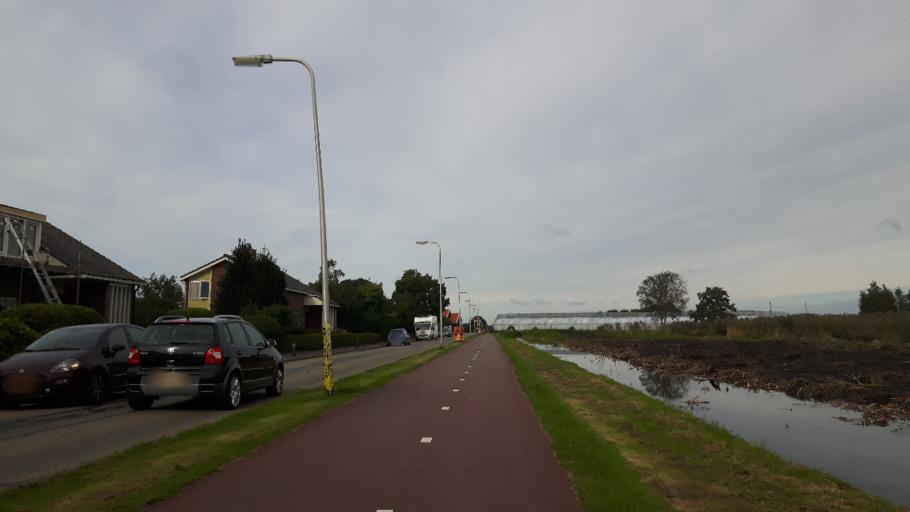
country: NL
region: Utrecht
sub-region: Gemeente De Ronde Venen
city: Mijdrecht
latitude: 52.1676
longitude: 4.8293
